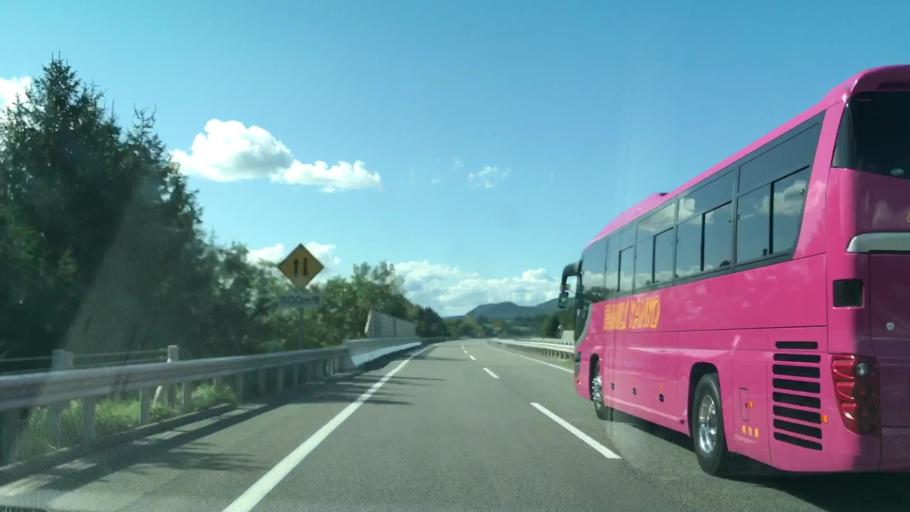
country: JP
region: Hokkaido
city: Date
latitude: 42.4882
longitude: 140.8844
